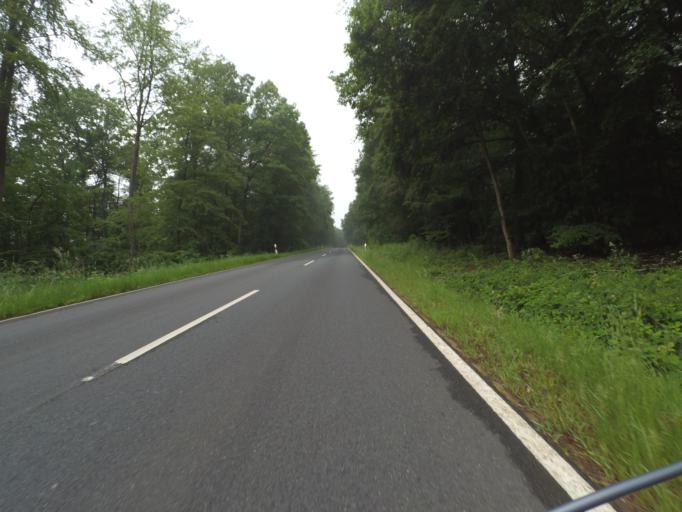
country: DE
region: Rheinland-Pfalz
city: Ernst
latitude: 50.1506
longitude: 7.2316
